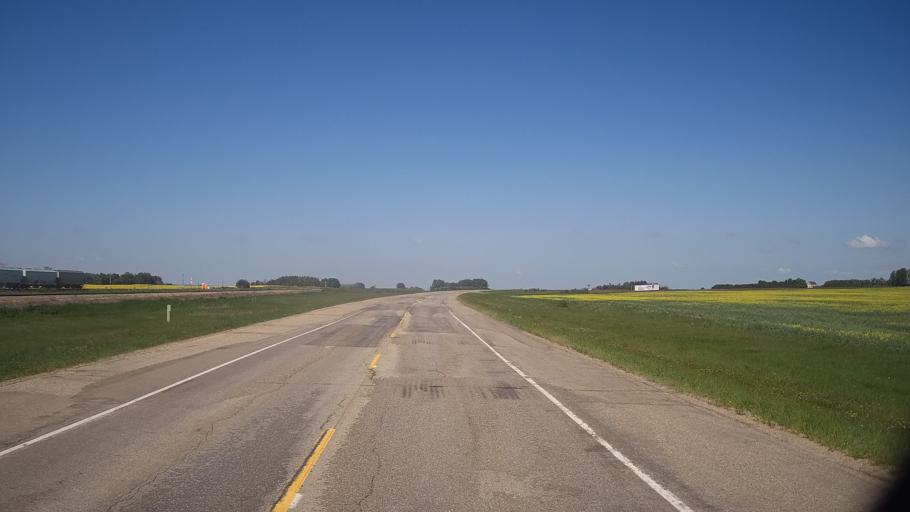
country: CA
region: Saskatchewan
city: Saskatoon
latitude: 51.9943
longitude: -106.0945
